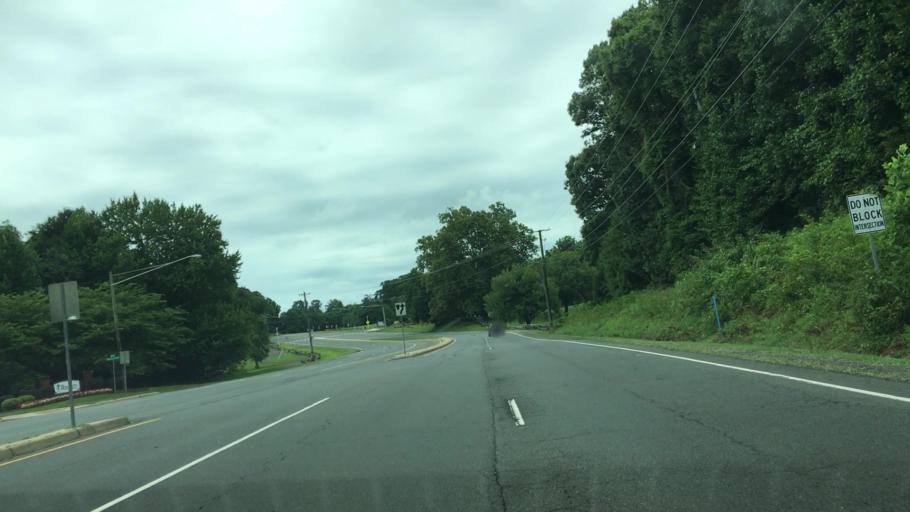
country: US
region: Virginia
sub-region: Prince William County
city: Buckhall
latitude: 38.7565
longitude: -77.4372
